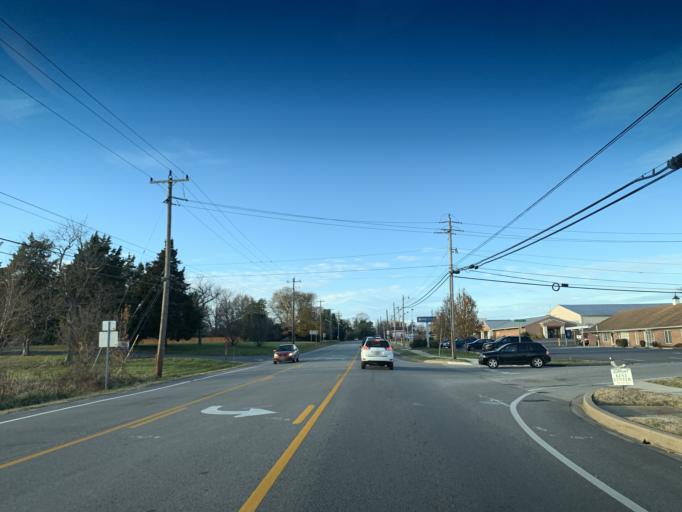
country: US
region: Maryland
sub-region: Kent County
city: Chestertown
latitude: 39.2257
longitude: -76.0711
